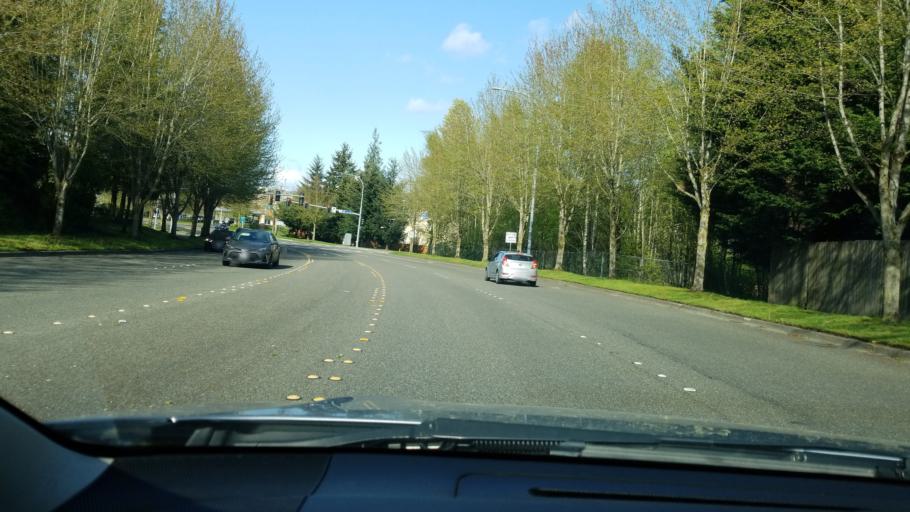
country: US
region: Washington
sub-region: Snohomish County
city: Alderwood Manor
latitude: 47.8189
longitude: -122.2725
